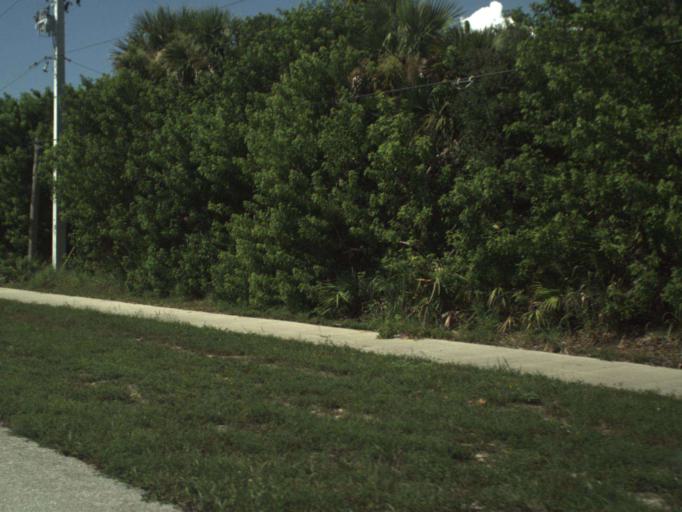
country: US
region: Florida
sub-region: Indian River County
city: Wabasso Beach
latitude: 27.7964
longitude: -80.4158
